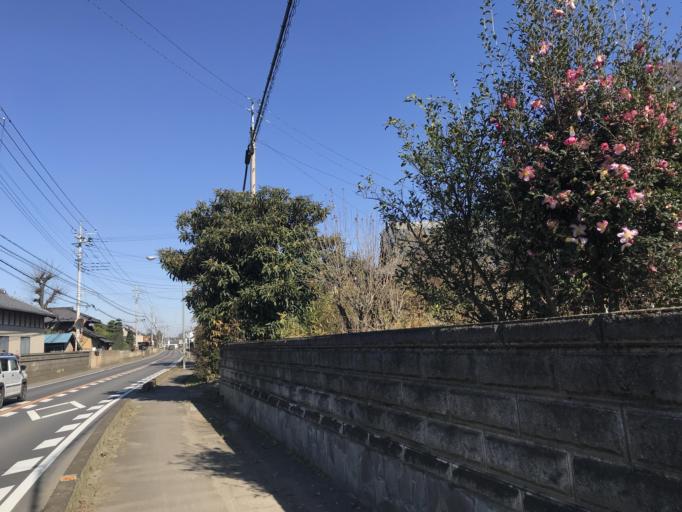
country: JP
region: Tochigi
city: Oyama
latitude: 36.2622
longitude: 139.8399
